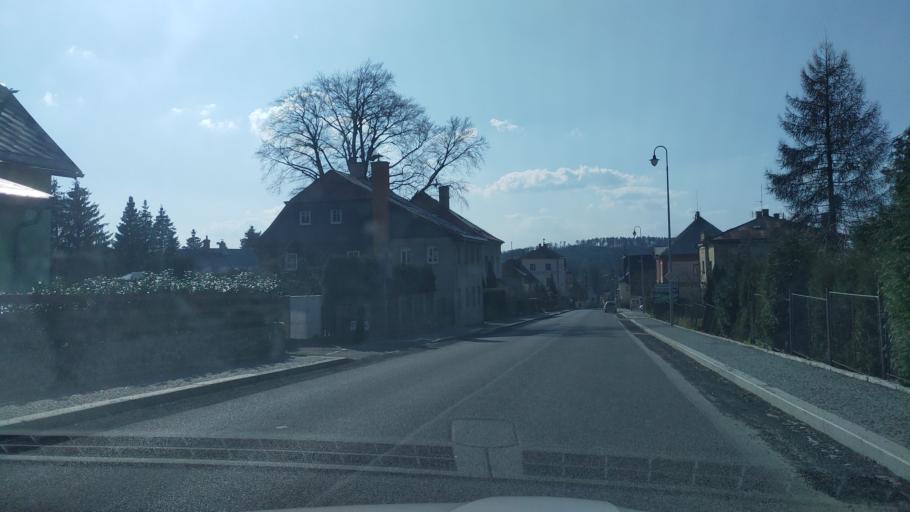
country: CZ
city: Kamenicky Senov
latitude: 50.7720
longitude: 14.4768
